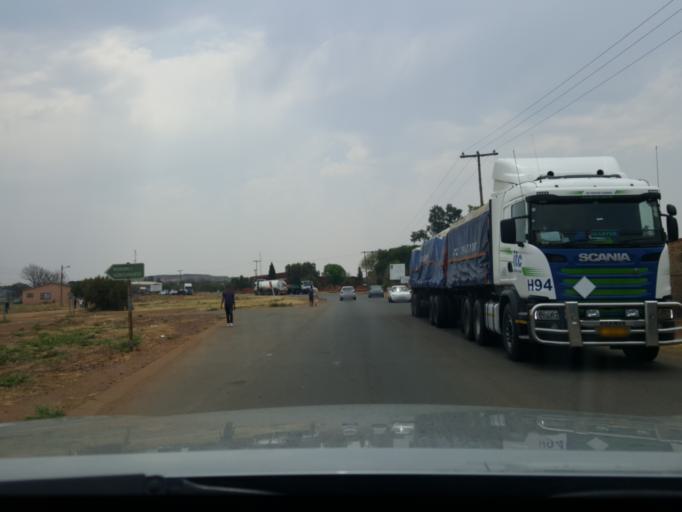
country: ZA
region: North-West
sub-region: Ngaka Modiri Molema District Municipality
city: Zeerust
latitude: -25.4891
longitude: 25.9842
